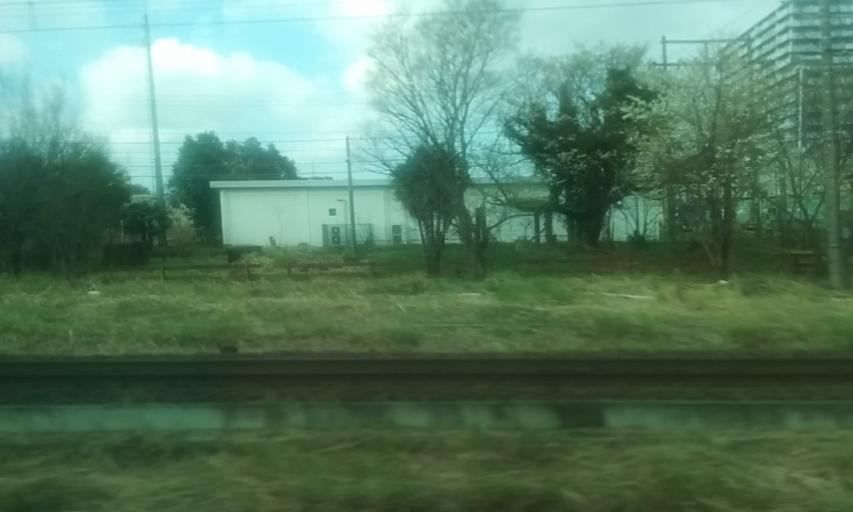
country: JP
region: Kanagawa
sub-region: Kawasaki-shi
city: Kawasaki
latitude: 35.5479
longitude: 139.6734
